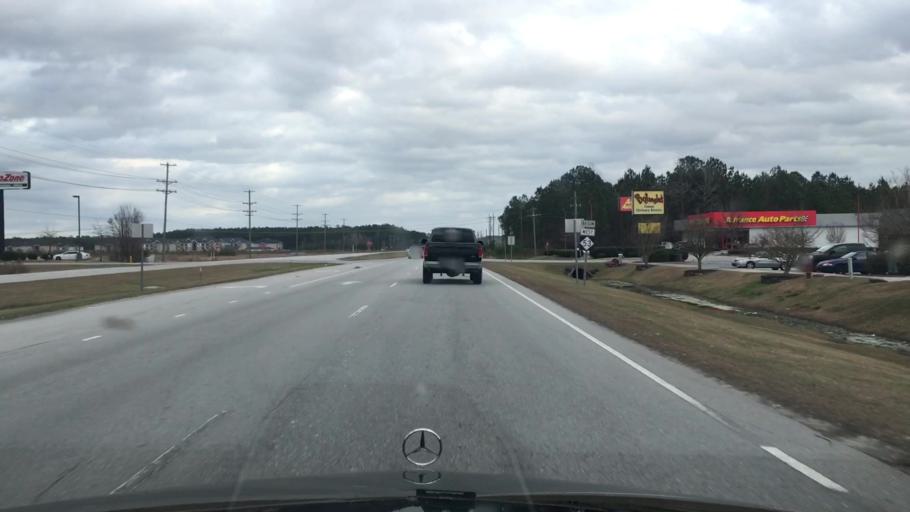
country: US
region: North Carolina
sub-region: Onslow County
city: Half Moon
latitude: 34.7996
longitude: -77.4378
